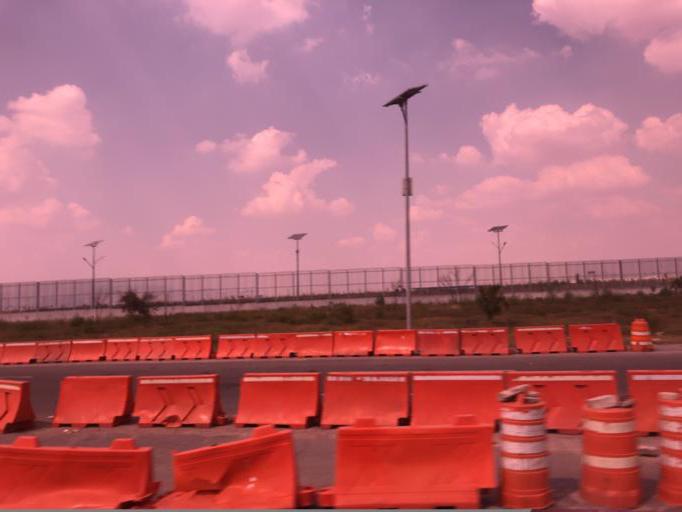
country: MX
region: Mexico
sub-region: Ciudad Nezahualcoyotl
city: Poligonos
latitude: 19.4783
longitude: -98.9801
